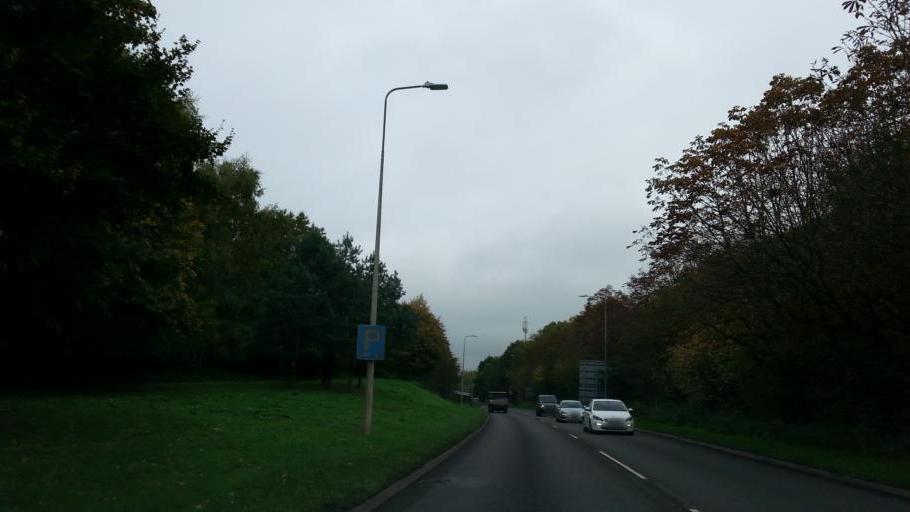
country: GB
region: England
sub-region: Worcestershire
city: Bromsgrove
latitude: 52.3360
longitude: -2.0472
